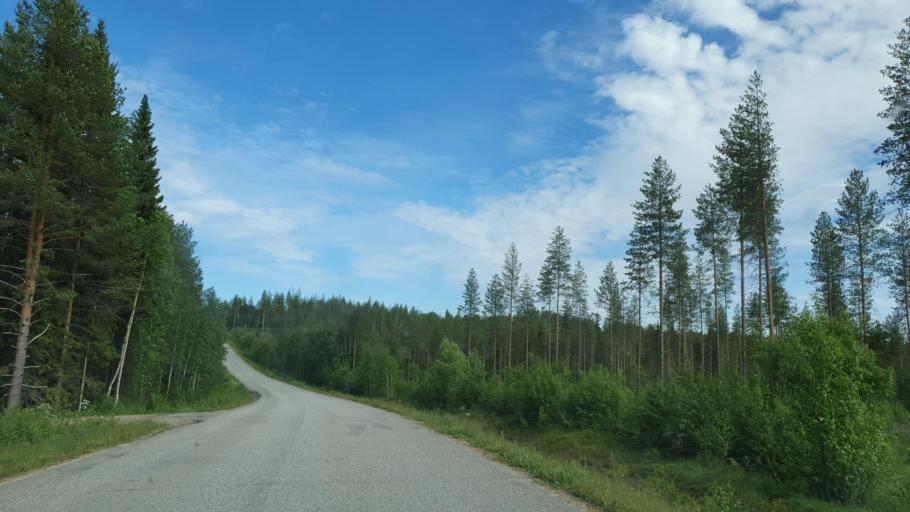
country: FI
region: Kainuu
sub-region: Kehys-Kainuu
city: Suomussalmi
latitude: 64.5525
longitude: 29.1874
